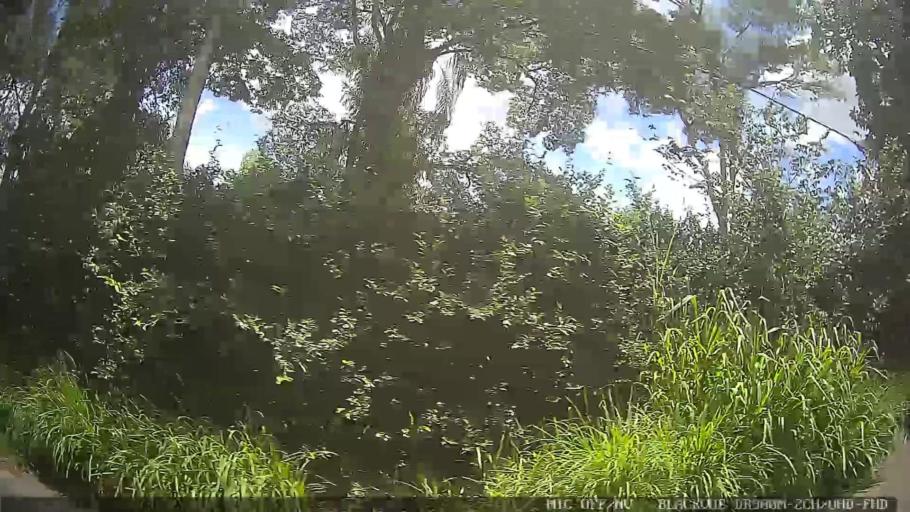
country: BR
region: Sao Paulo
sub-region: Braganca Paulista
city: Braganca Paulista
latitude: -22.9204
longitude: -46.5663
